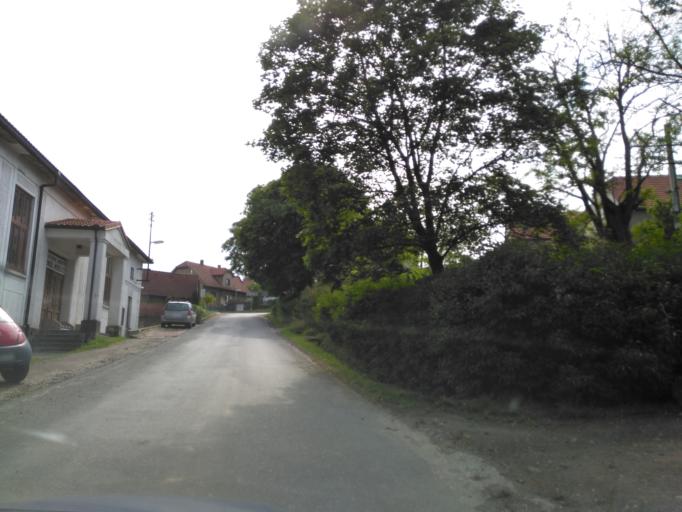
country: CZ
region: Central Bohemia
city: Hudlice
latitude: 49.9618
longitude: 13.9700
